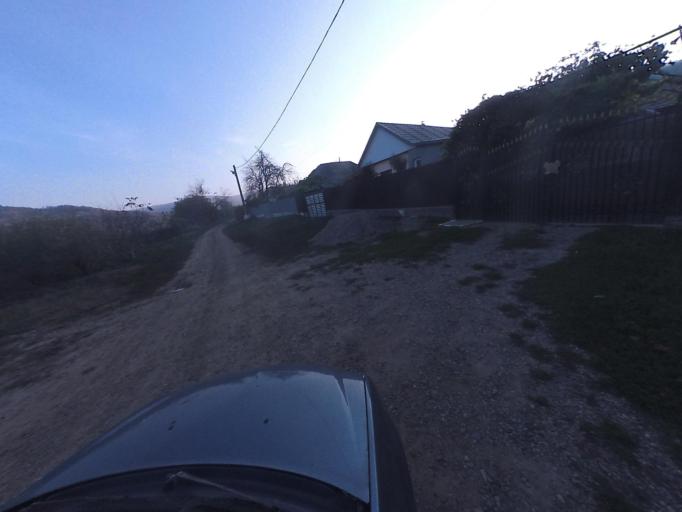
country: RO
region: Vaslui
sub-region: Comuna Bacesti
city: Bacesti
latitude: 46.7983
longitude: 27.2254
